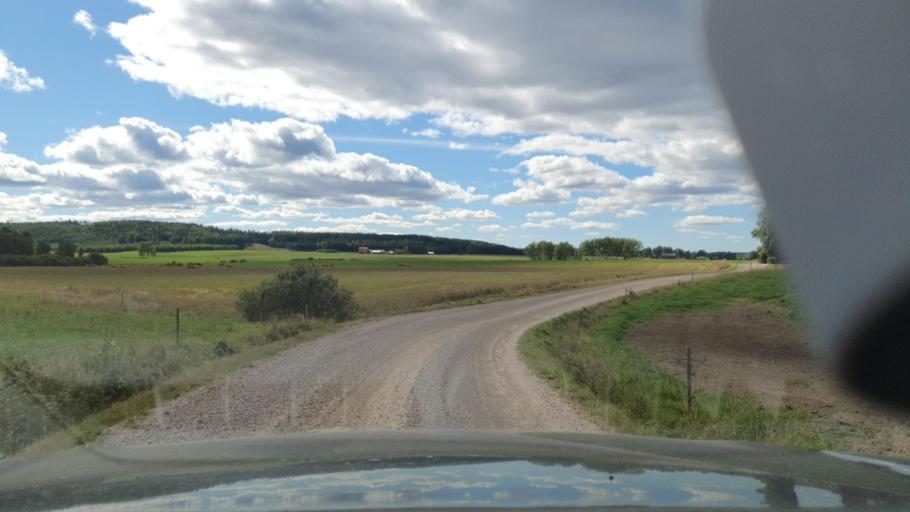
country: SE
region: Vaermland
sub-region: Karlstads Kommun
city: Molkom
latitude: 59.5600
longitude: 13.7218
